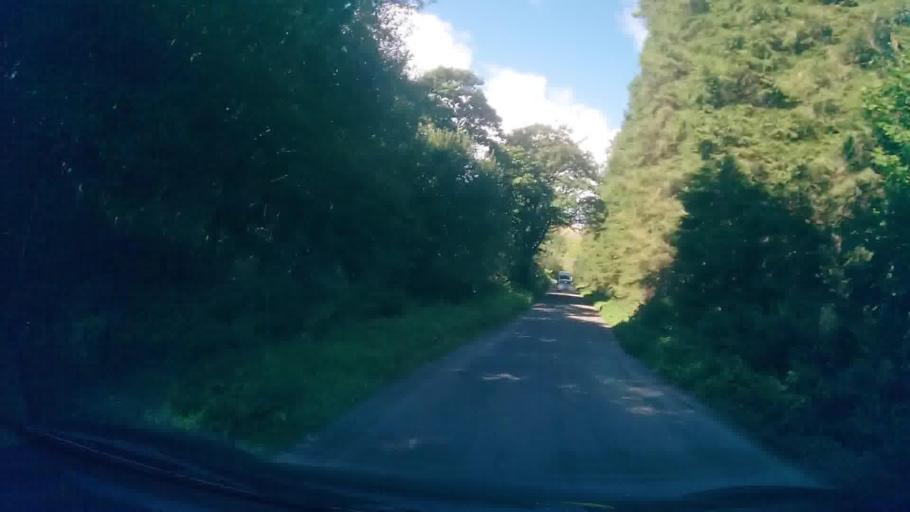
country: GB
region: Wales
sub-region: Merthyr Tydfil County Borough
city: Merthyr Tydfil
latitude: 51.8358
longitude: -3.3830
